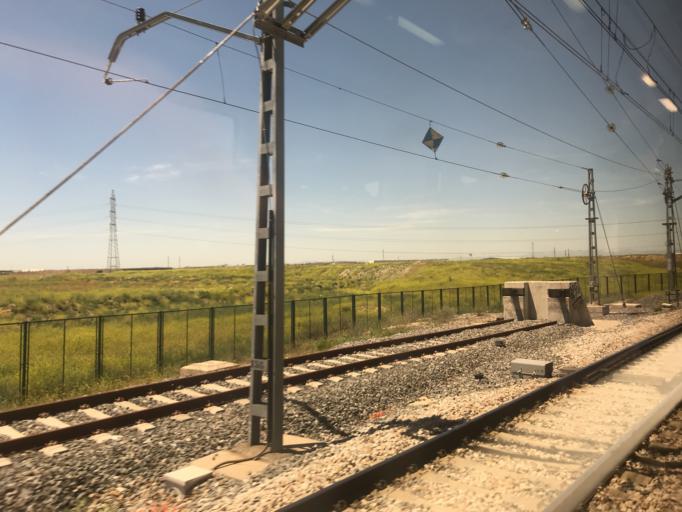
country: ES
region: Madrid
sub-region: Provincia de Madrid
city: Pinto
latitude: 40.2595
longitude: -3.7044
